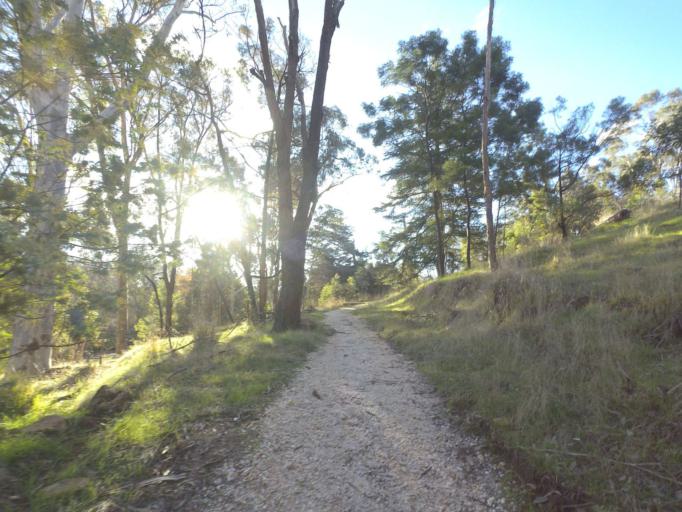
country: AU
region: Victoria
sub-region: Mount Alexander
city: Castlemaine
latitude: -37.1610
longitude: 144.2146
